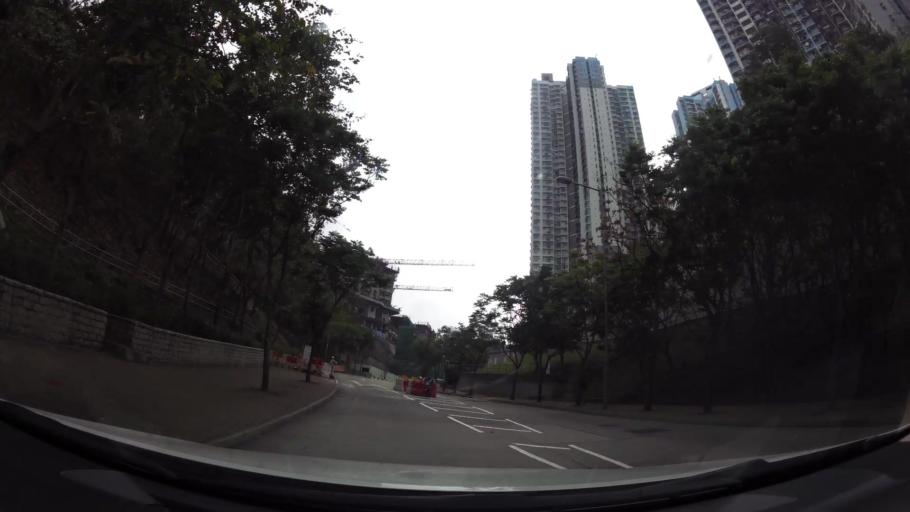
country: HK
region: Kowloon City
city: Kowloon
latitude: 22.3310
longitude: 114.2120
